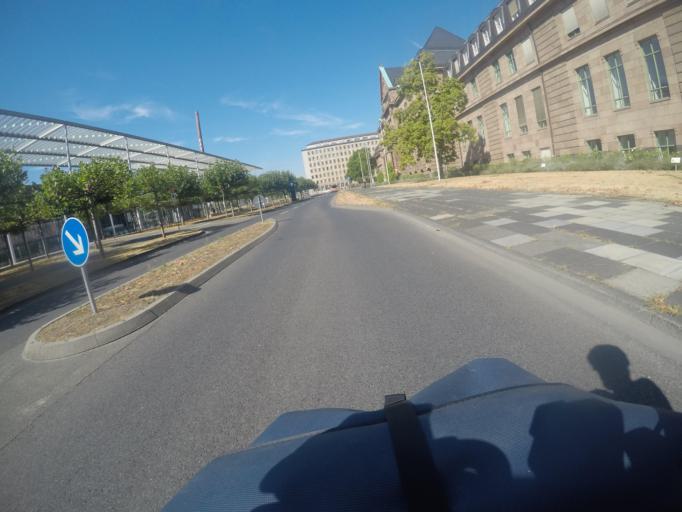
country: DE
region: North Rhine-Westphalia
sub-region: Regierungsbezirk Koln
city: Leverkusen
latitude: 51.0143
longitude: 6.9841
